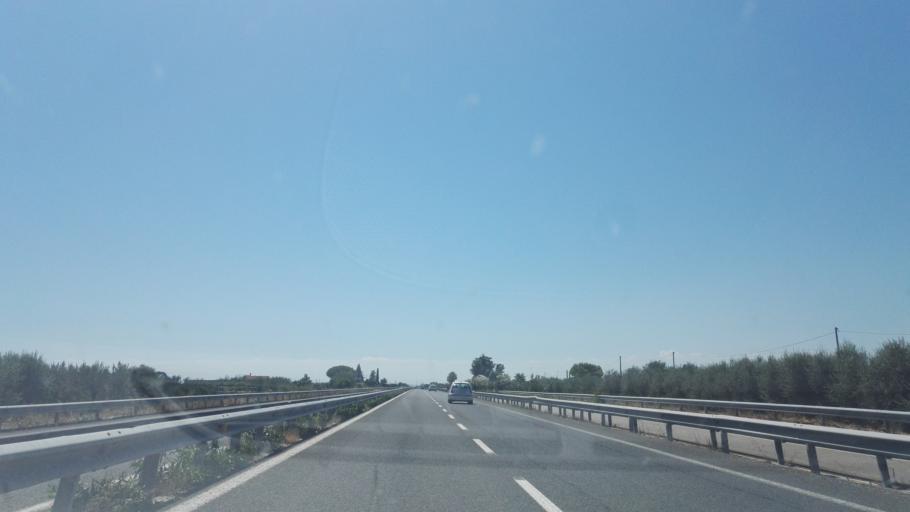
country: IT
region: Apulia
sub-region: Provincia di Taranto
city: Palagiano
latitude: 40.5085
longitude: 16.9825
